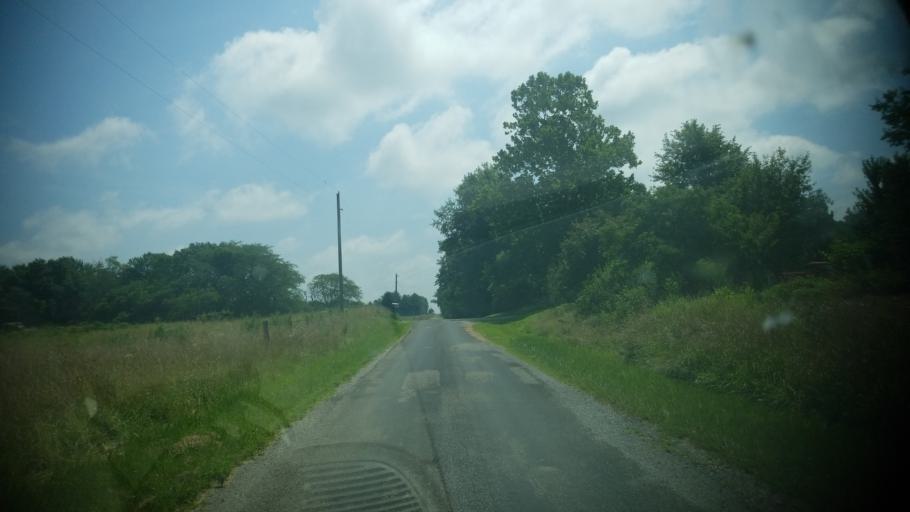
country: US
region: Illinois
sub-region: Wayne County
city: Fairfield
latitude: 38.5300
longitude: -88.3980
